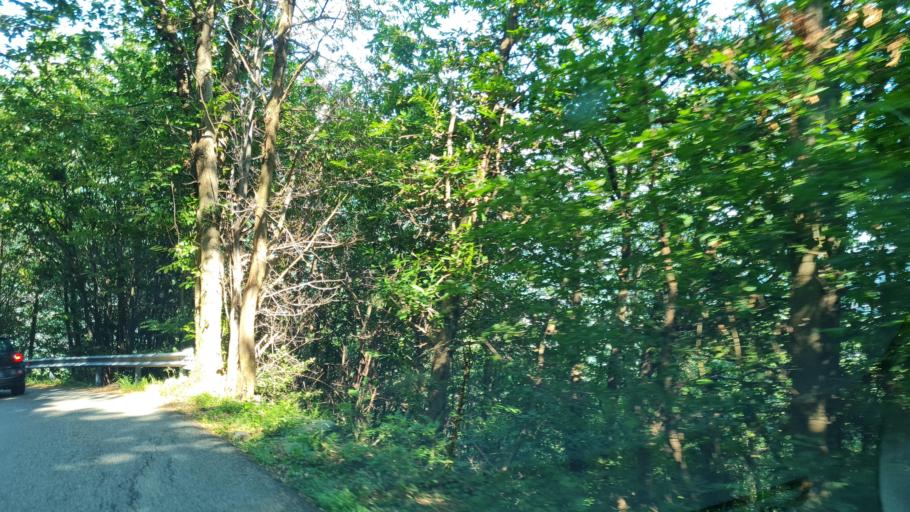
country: IT
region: Piedmont
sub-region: Provincia di Torino
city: Quincinetto
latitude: 45.5554
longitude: 7.8004
